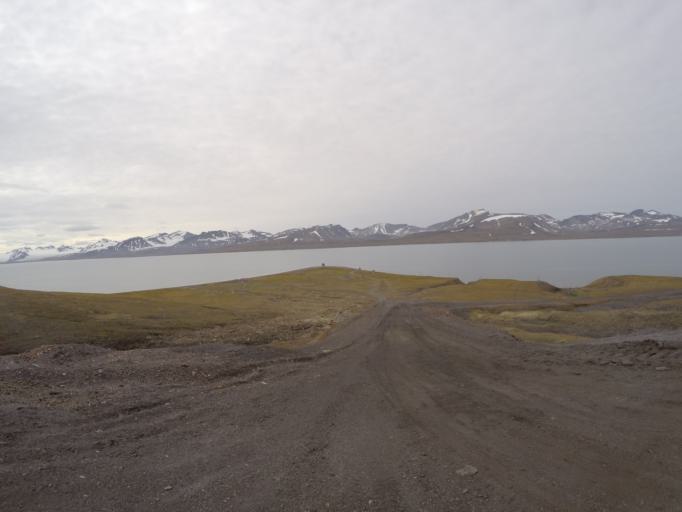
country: SJ
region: Svalbard
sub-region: Spitsbergen
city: Longyearbyen
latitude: 78.0462
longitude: 14.2296
